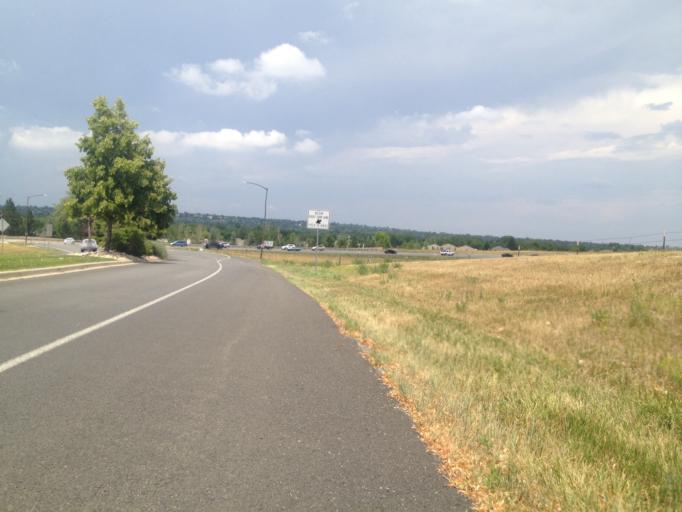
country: US
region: Colorado
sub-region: Boulder County
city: Superior
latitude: 39.9548
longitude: -105.1469
